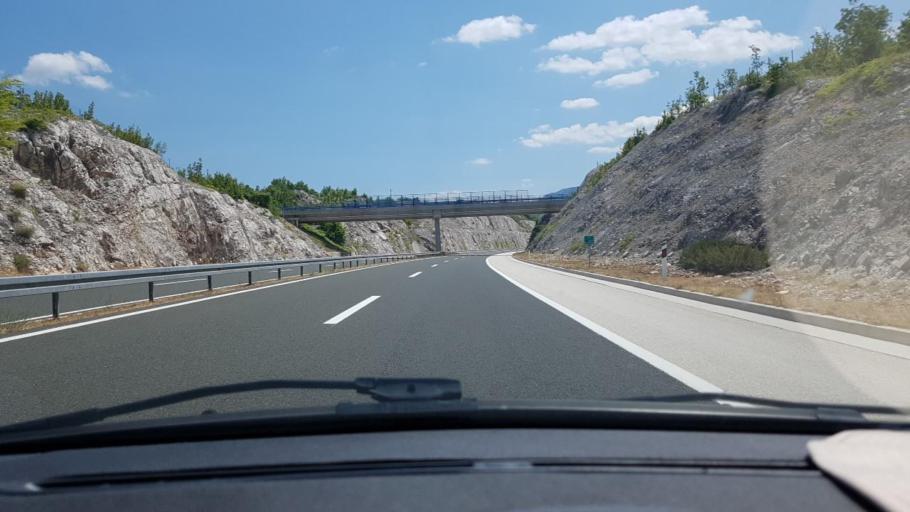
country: HR
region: Splitsko-Dalmatinska
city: Grubine
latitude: 43.3742
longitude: 17.0887
